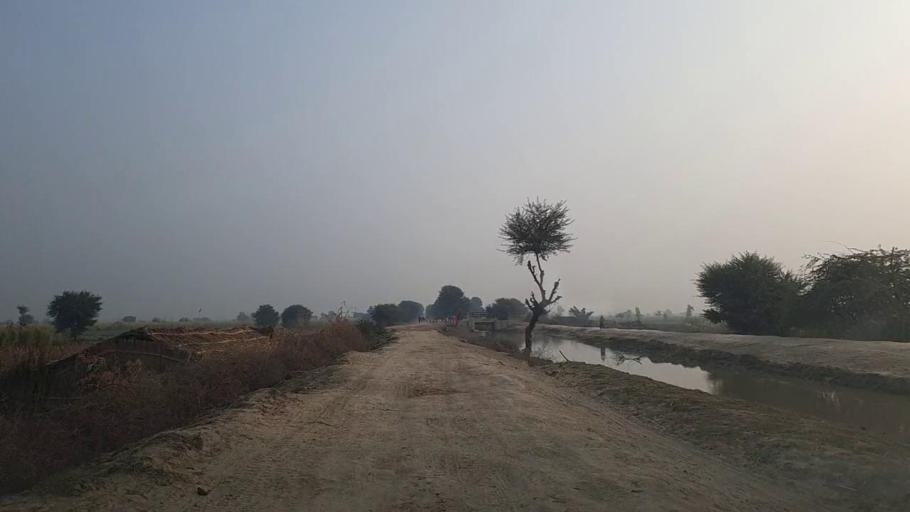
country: PK
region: Sindh
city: Khadro
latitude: 26.1224
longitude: 68.8016
